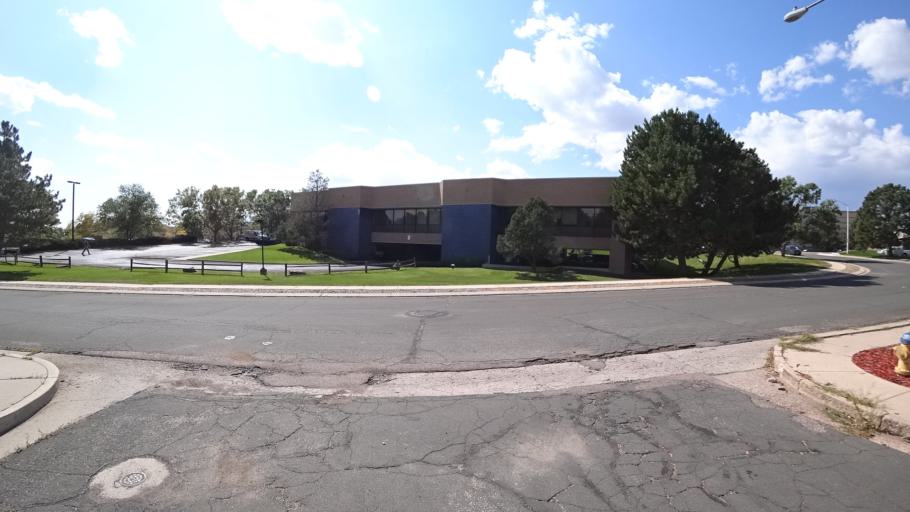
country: US
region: Colorado
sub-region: El Paso County
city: Cimarron Hills
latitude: 38.8782
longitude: -104.7536
